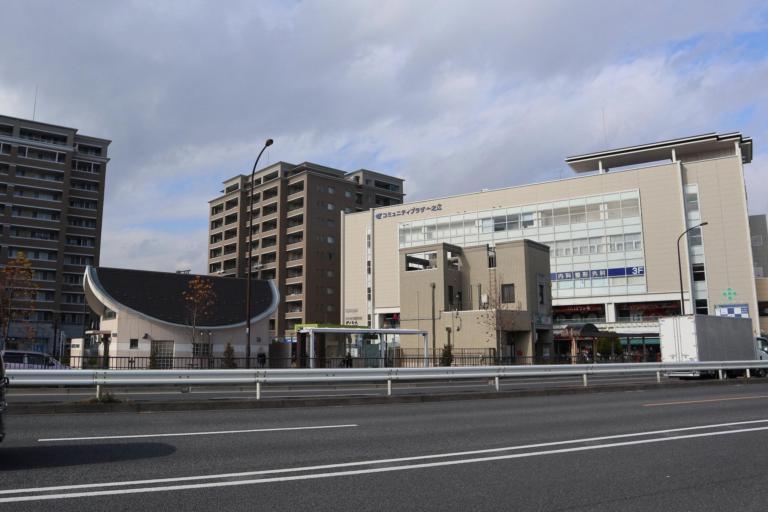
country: JP
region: Tokyo
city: Urayasu
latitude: 35.6853
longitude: 139.8822
